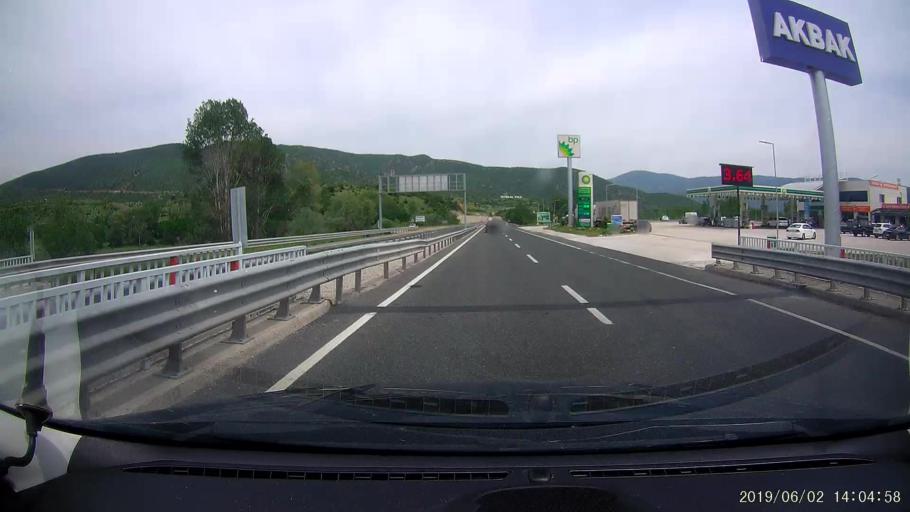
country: TR
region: Cankiri
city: Ilgaz
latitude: 40.9032
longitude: 33.6608
